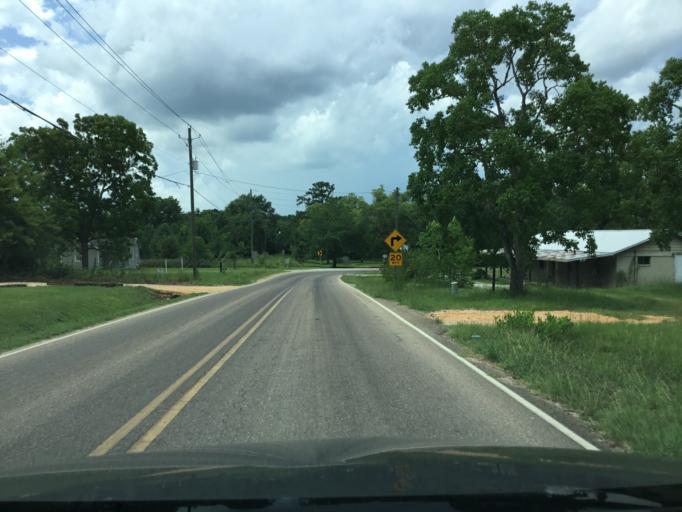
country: US
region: Alabama
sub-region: Montgomery County
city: Pike Road
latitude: 32.3637
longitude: -86.1032
